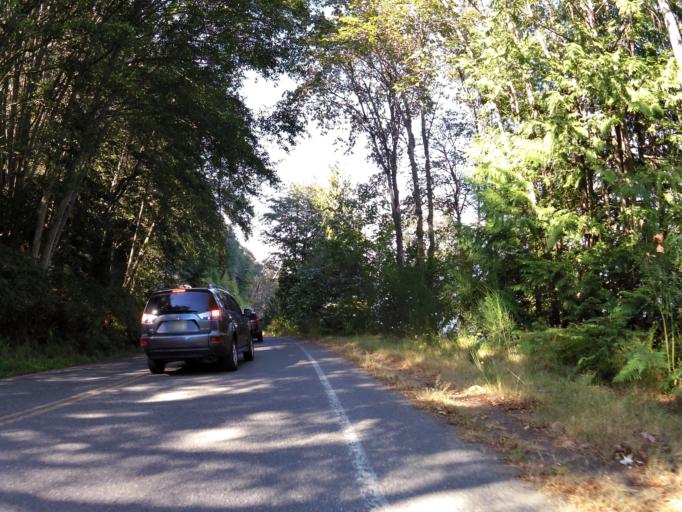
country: CA
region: British Columbia
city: North Saanich
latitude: 48.6187
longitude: -123.5225
